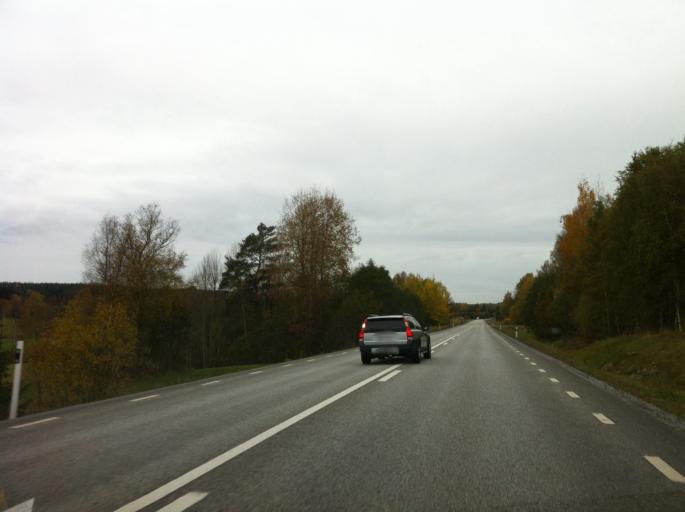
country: SE
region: OErebro
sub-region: Ljusnarsbergs Kommun
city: Kopparberg
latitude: 59.8402
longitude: 15.0850
